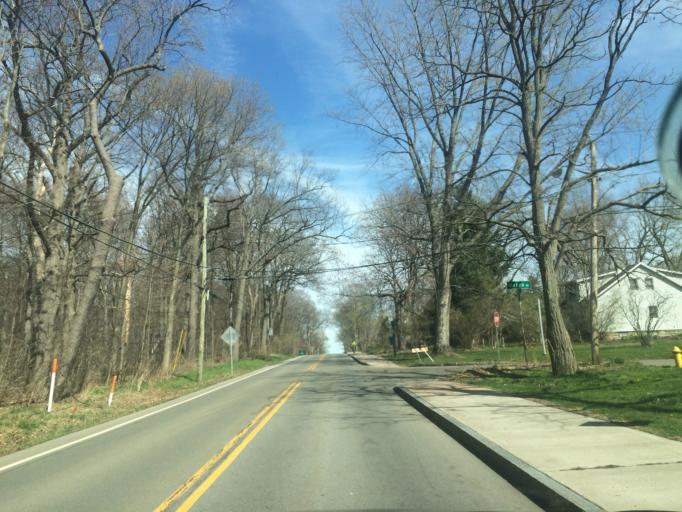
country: US
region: New York
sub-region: Monroe County
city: Rochester
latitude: 43.1138
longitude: -77.6412
